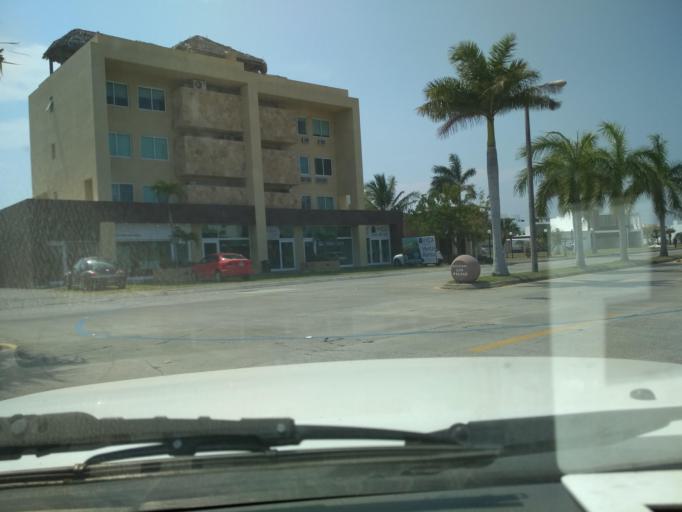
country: MX
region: Veracruz
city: Boca del Rio
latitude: 19.0991
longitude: -96.1158
